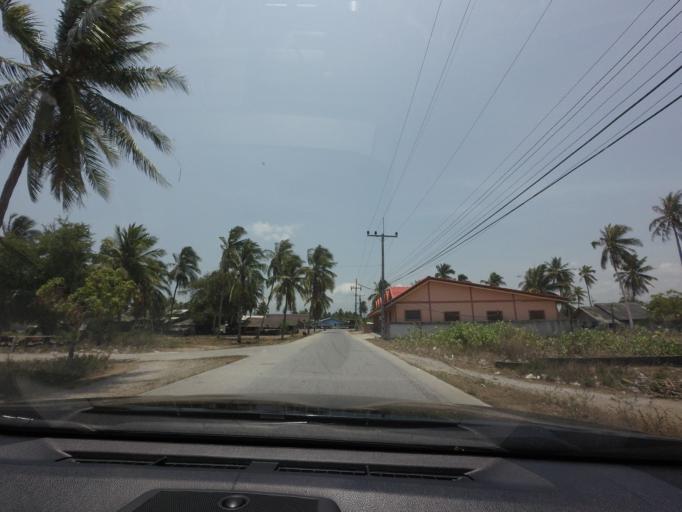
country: TH
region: Pattani
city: Yaring
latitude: 6.8968
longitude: 101.3736
